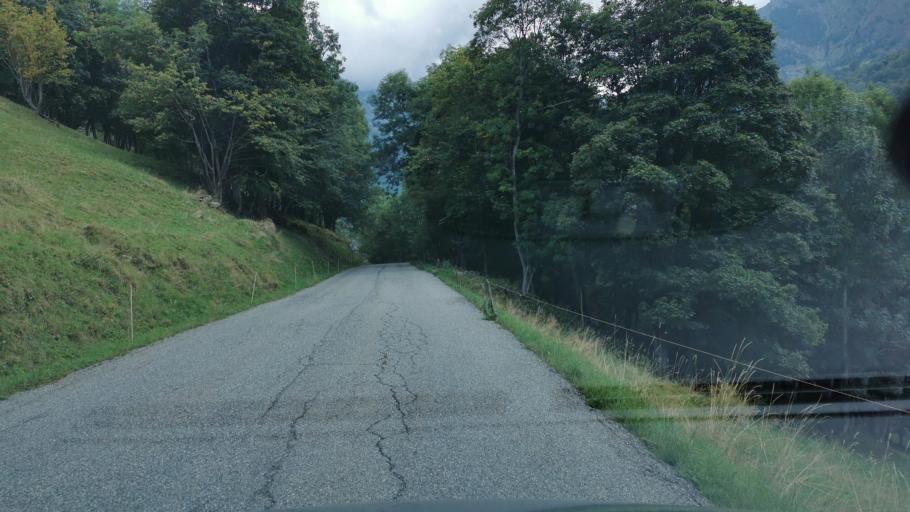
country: IT
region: Piedmont
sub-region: Provincia di Torino
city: Usseglio
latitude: 45.2269
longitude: 7.2048
